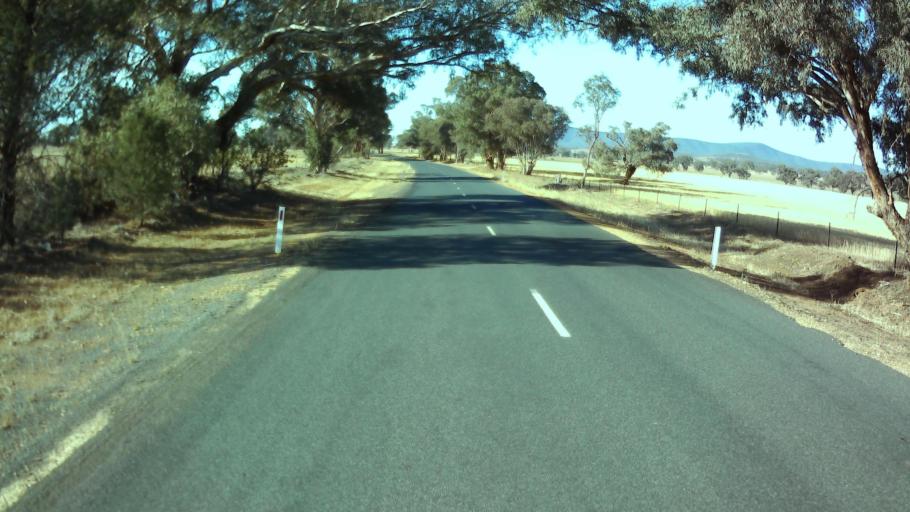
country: AU
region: New South Wales
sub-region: Weddin
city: Grenfell
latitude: -33.9227
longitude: 148.1395
